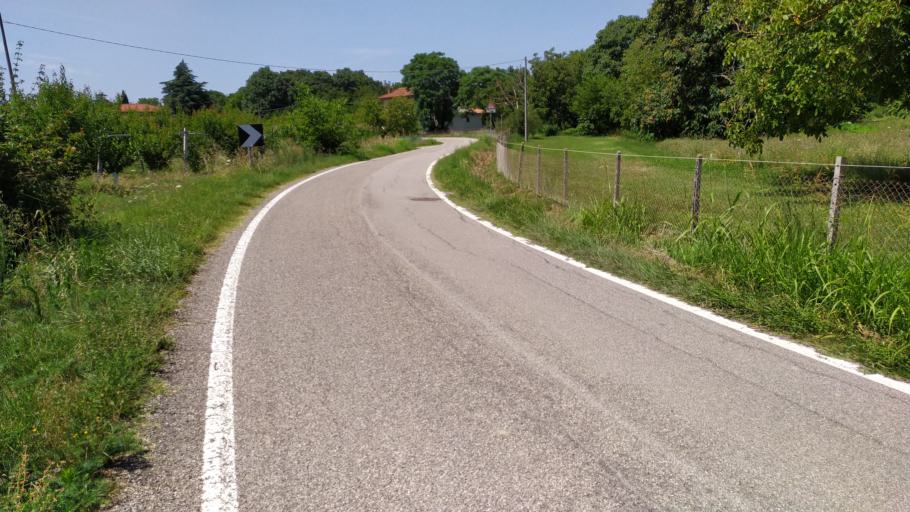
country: IT
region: Emilia-Romagna
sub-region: Forli-Cesena
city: Castrocaro Terme e Terra del Sole
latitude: 44.2006
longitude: 11.9862
